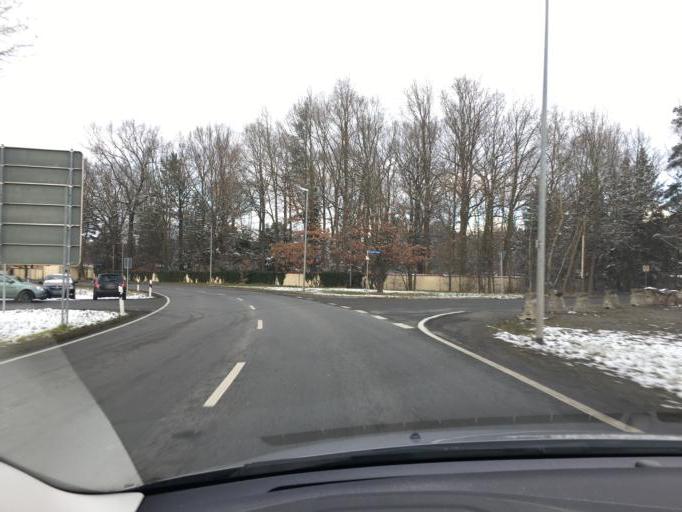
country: DE
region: Saxony
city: Brandis
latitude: 51.3081
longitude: 12.6004
